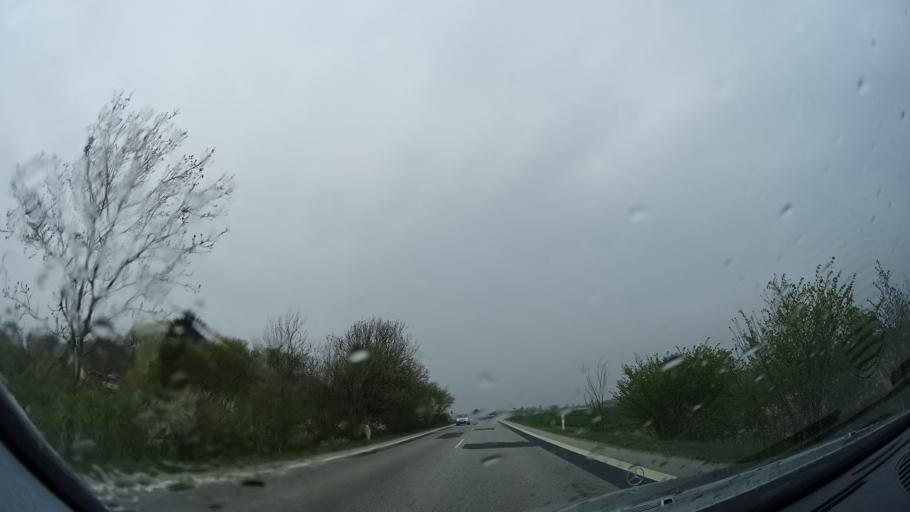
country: DK
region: Zealand
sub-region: Holbaek Kommune
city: Vipperod
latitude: 55.6955
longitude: 11.7844
